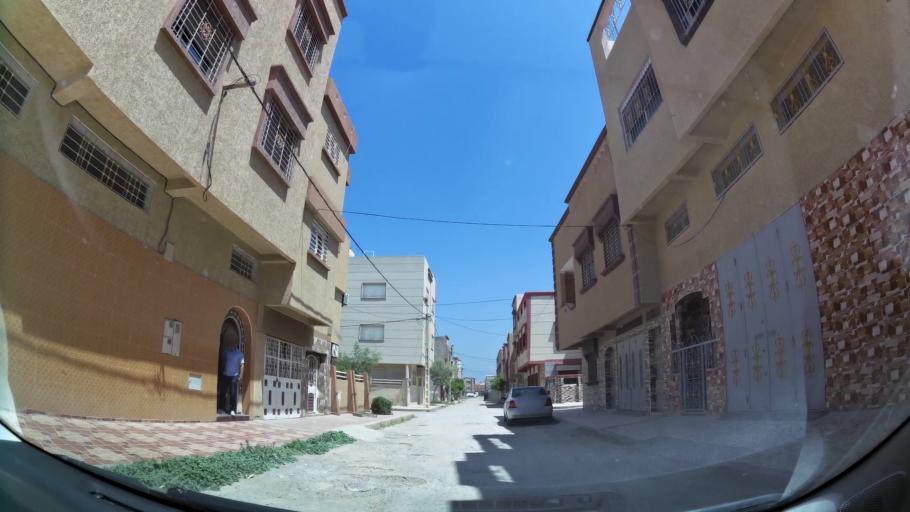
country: MA
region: Oriental
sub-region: Oujda-Angad
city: Oujda
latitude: 34.6957
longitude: -1.8895
